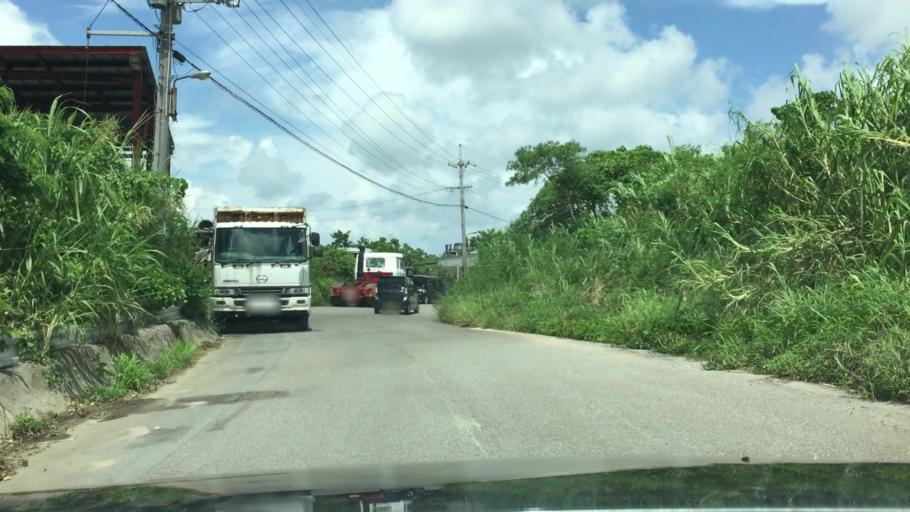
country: JP
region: Okinawa
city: Ishigaki
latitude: 24.3594
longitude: 124.1555
